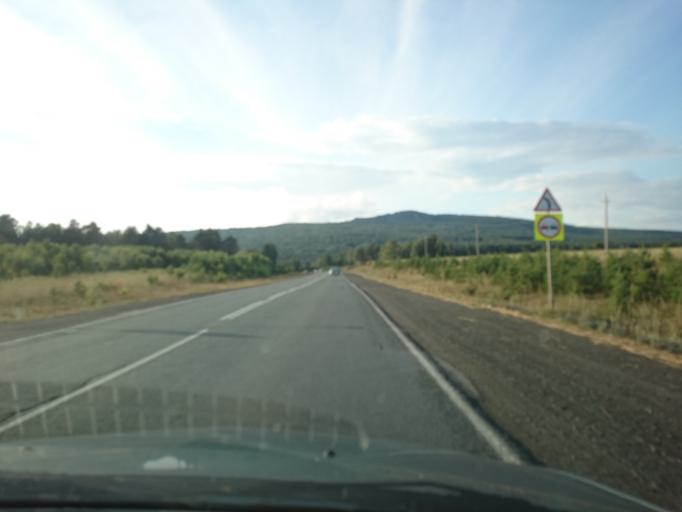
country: RU
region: Bashkortostan
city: Lomovka
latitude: 53.8924
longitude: 58.0941
